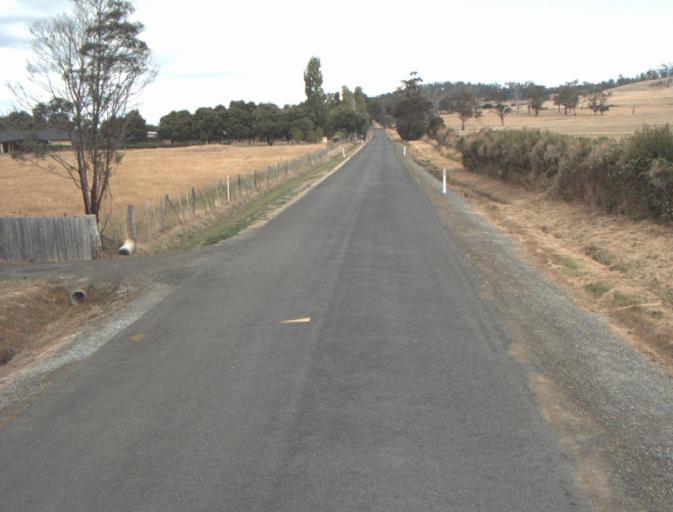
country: AU
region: Tasmania
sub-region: Launceston
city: Mayfield
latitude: -41.2865
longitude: 146.9988
